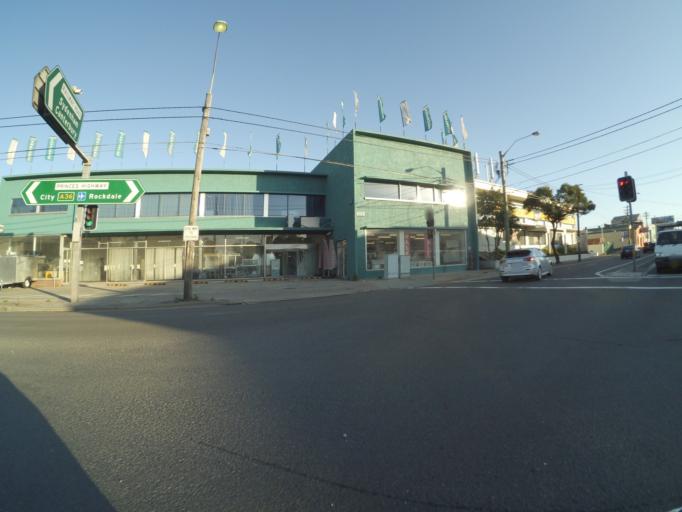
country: AU
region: New South Wales
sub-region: Marrickville
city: Newtown
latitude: -33.9191
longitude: 151.1692
